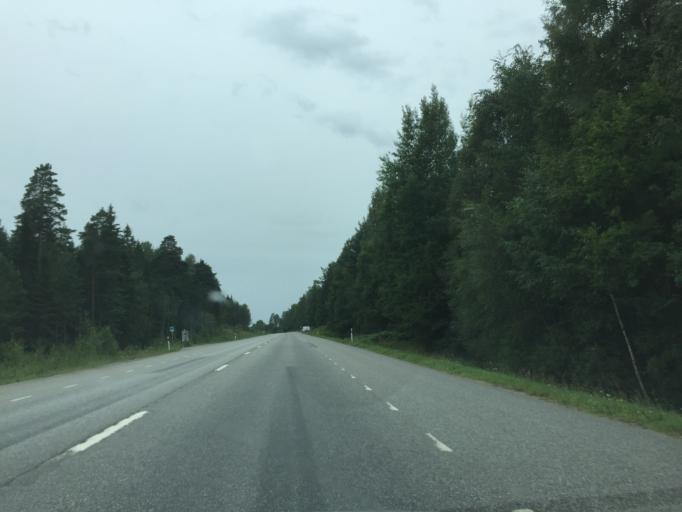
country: SE
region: OErebro
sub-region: Orebro Kommun
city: Orebro
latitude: 59.2333
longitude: 15.2292
